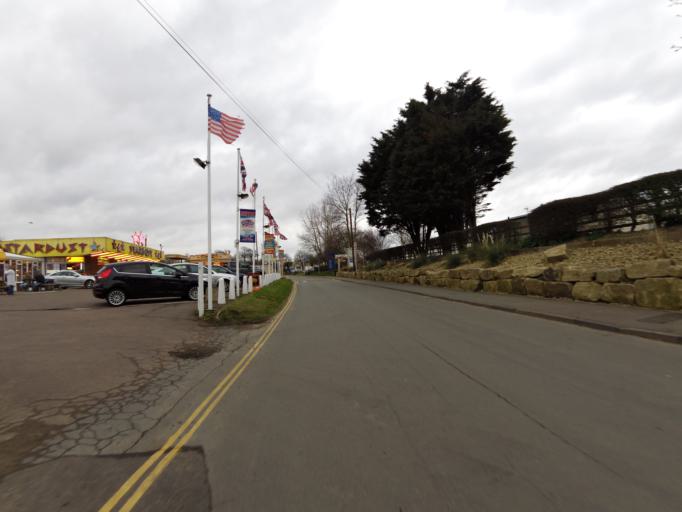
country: GB
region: England
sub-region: Norfolk
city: Hopton on Sea
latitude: 52.5402
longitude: 1.7323
